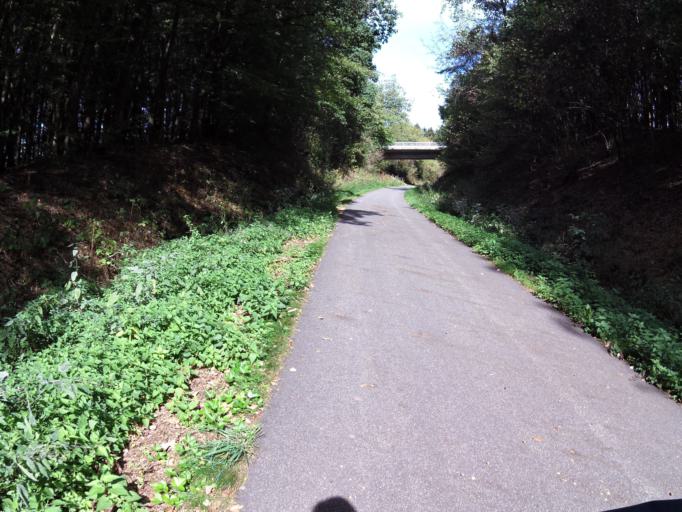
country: DE
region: Rheinland-Pfalz
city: Arzfeld
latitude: 50.1040
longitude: 6.2717
